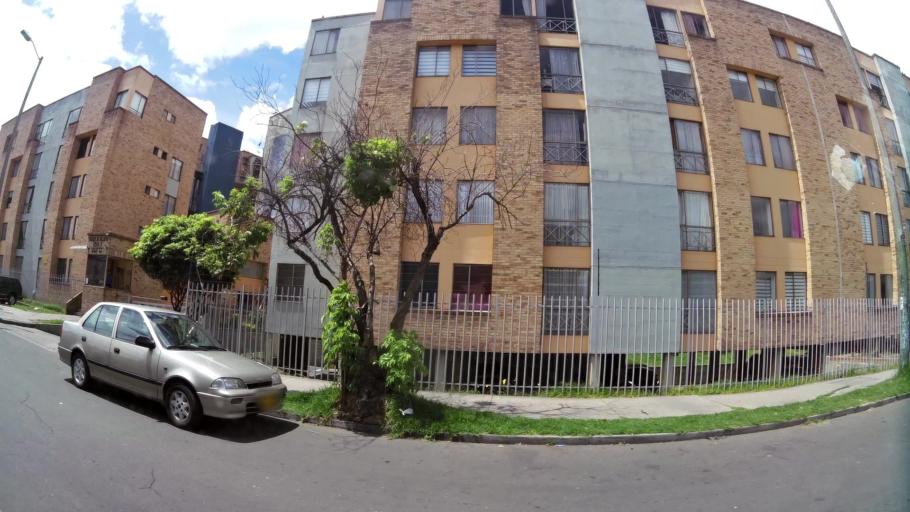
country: CO
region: Bogota D.C.
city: Bogota
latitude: 4.6183
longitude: -74.1253
